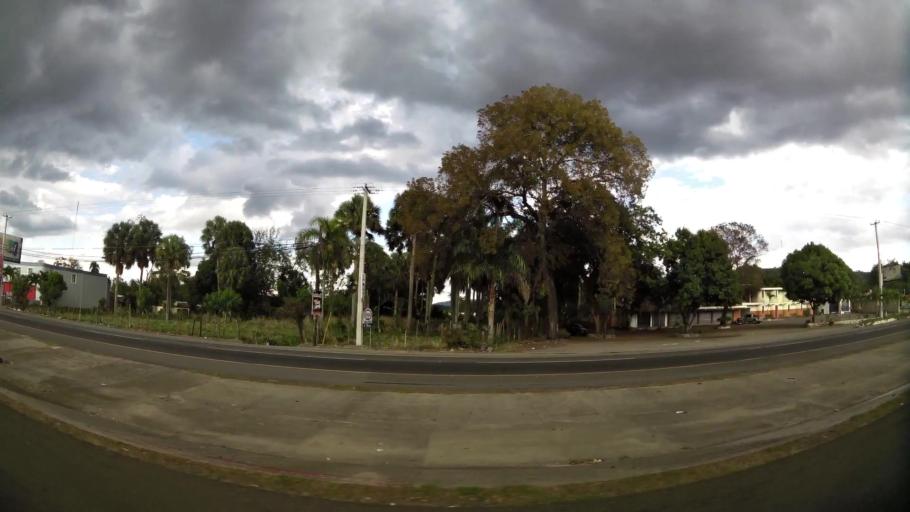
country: DO
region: Monsenor Nouel
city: Bonao
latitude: 18.9938
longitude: -70.4335
